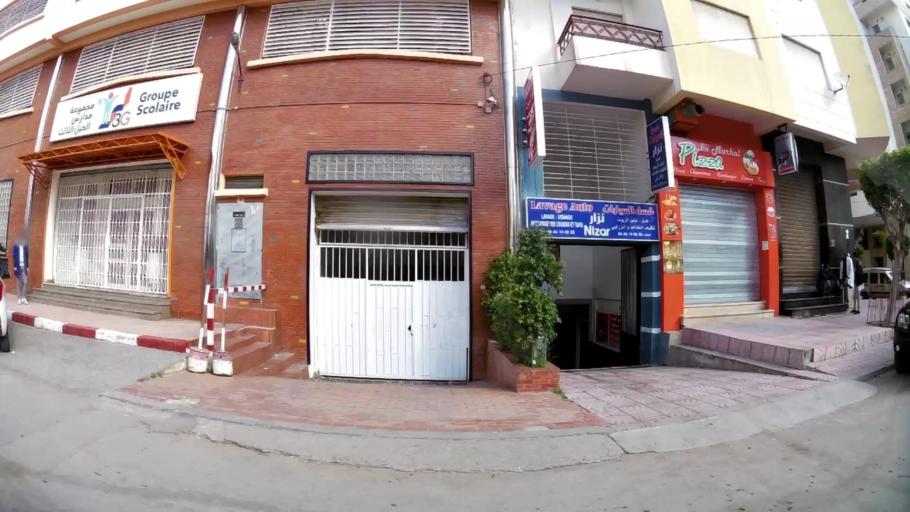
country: MA
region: Tanger-Tetouan
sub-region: Tanger-Assilah
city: Tangier
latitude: 35.7728
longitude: -5.7994
